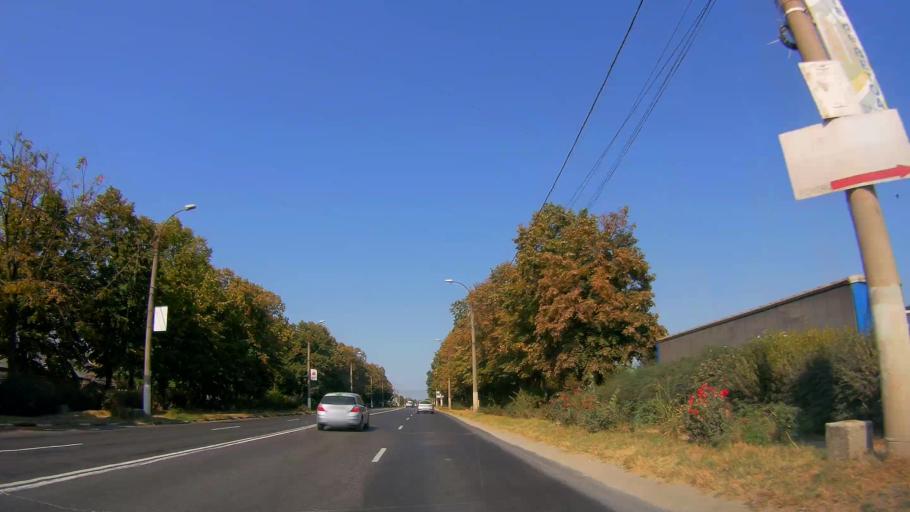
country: RO
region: Giurgiu
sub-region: Comuna Fratesti
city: Remus
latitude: 43.9289
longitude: 25.9754
